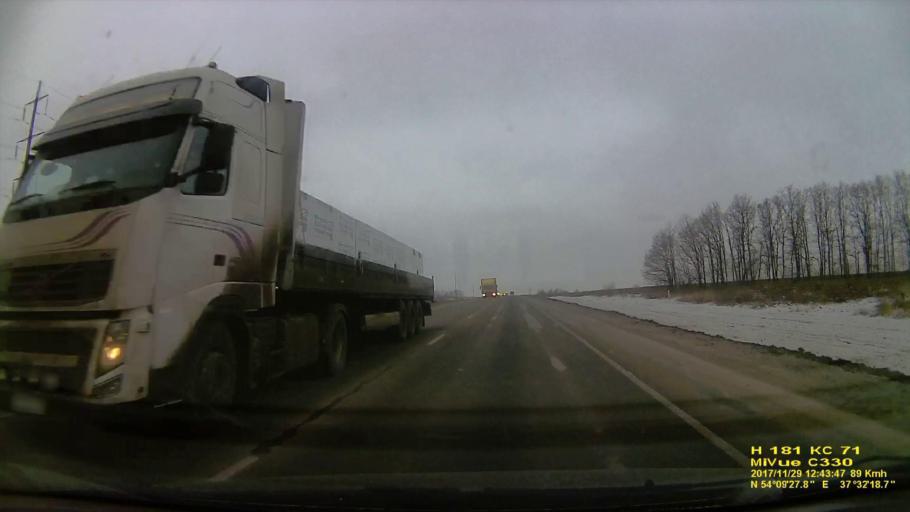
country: RU
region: Tula
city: Kosaya Gora
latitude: 54.1585
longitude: 37.5393
